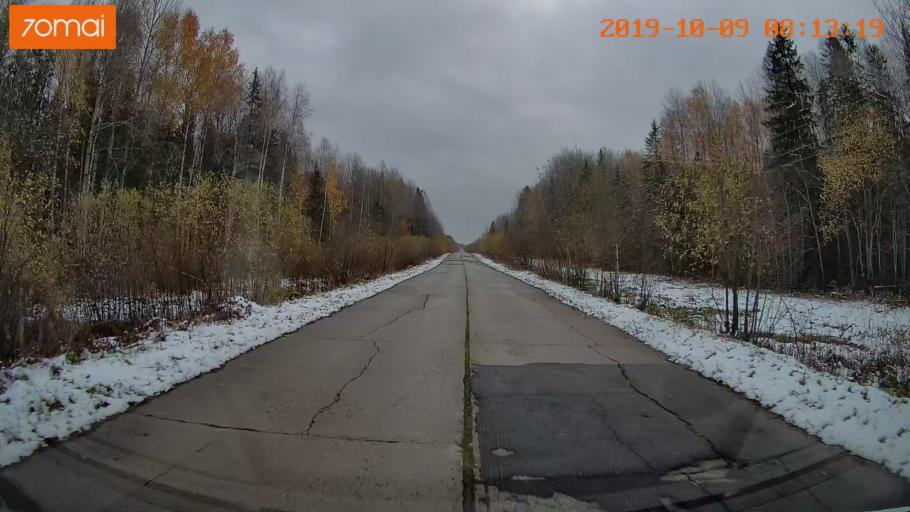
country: RU
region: Vologda
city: Gryazovets
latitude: 58.7229
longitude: 40.1380
